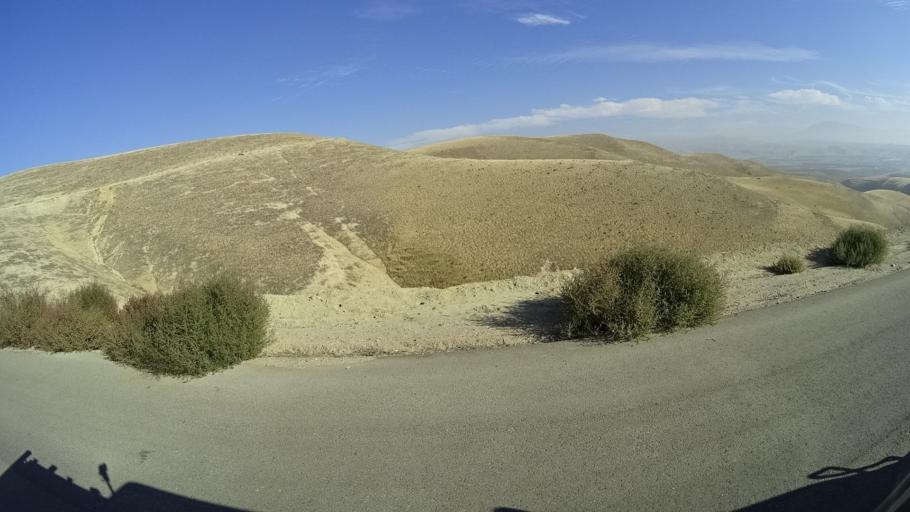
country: US
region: California
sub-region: Kern County
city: Oildale
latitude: 35.4678
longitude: -118.8708
